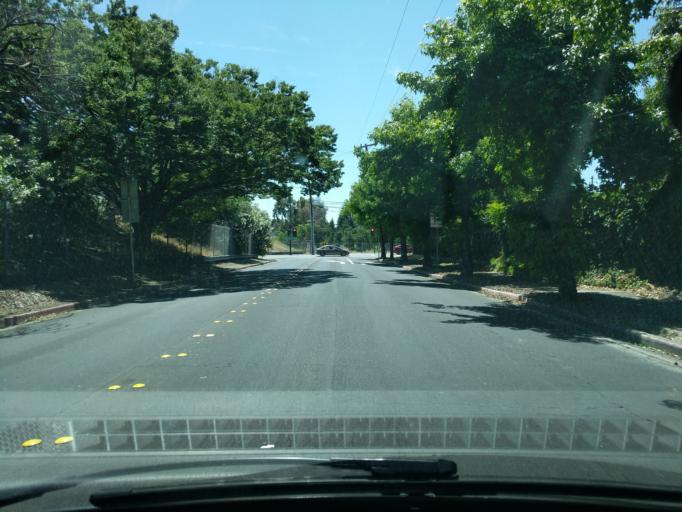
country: US
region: California
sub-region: Contra Costa County
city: Waldon
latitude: 37.9346
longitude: -122.0462
